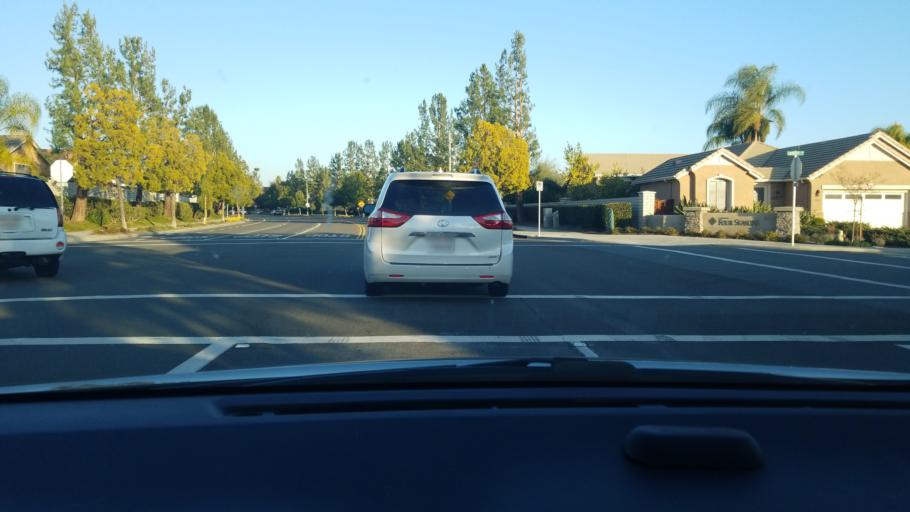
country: US
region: California
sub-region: Riverside County
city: Murrieta Hot Springs
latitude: 33.5443
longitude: -117.1354
